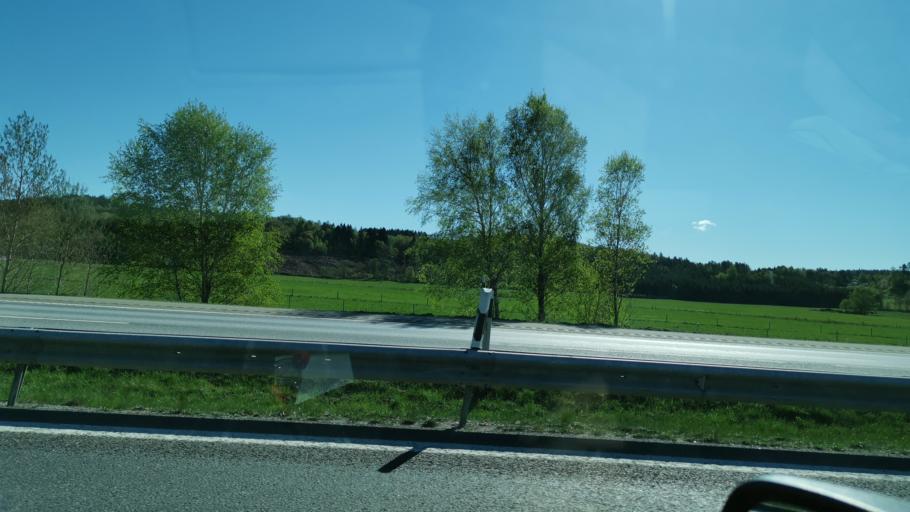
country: SE
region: Vaestra Goetaland
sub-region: Stenungsunds Kommun
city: Stenungsund
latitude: 58.0680
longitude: 11.8903
